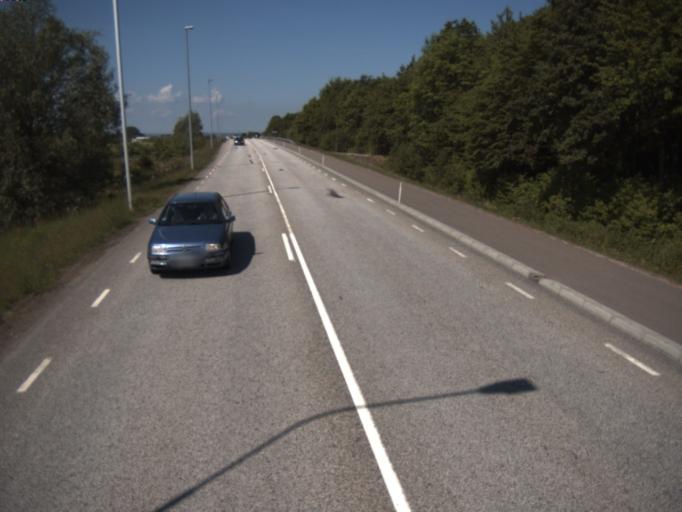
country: SE
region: Skane
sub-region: Helsingborg
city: Rydeback
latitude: 56.0020
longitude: 12.7579
